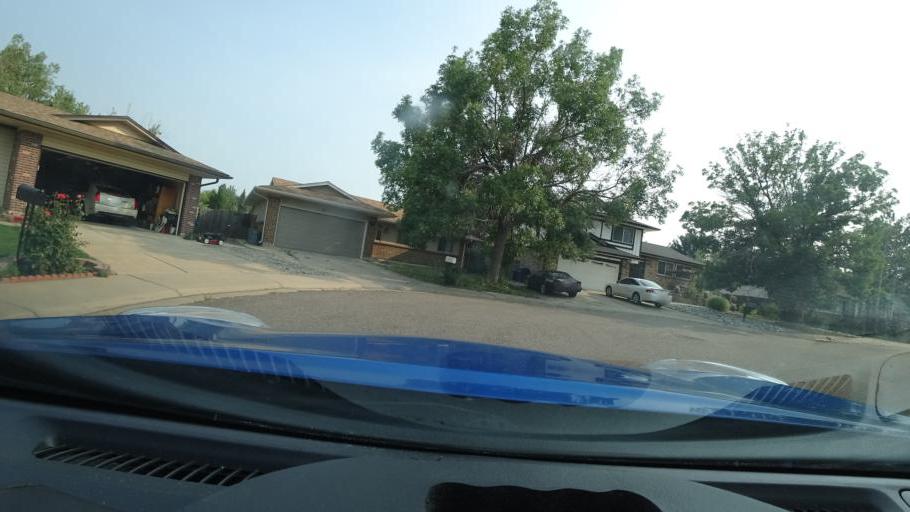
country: US
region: Colorado
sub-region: Adams County
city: Aurora
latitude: 39.6680
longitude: -104.7870
